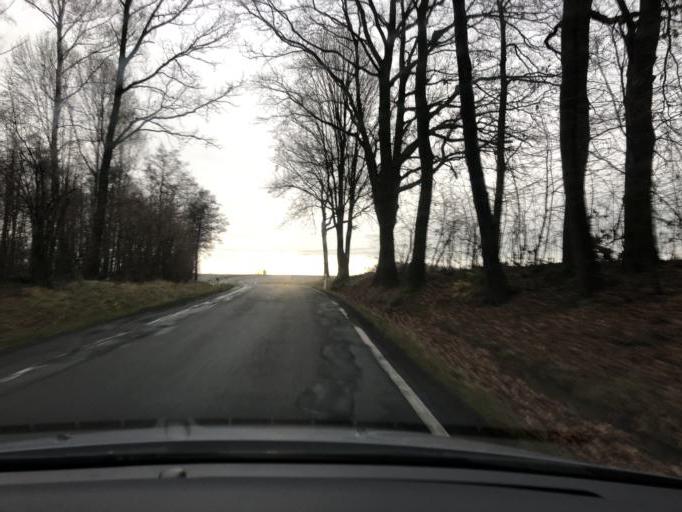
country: DE
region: Saxony
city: Niederfrohna
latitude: 50.8795
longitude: 12.7190
